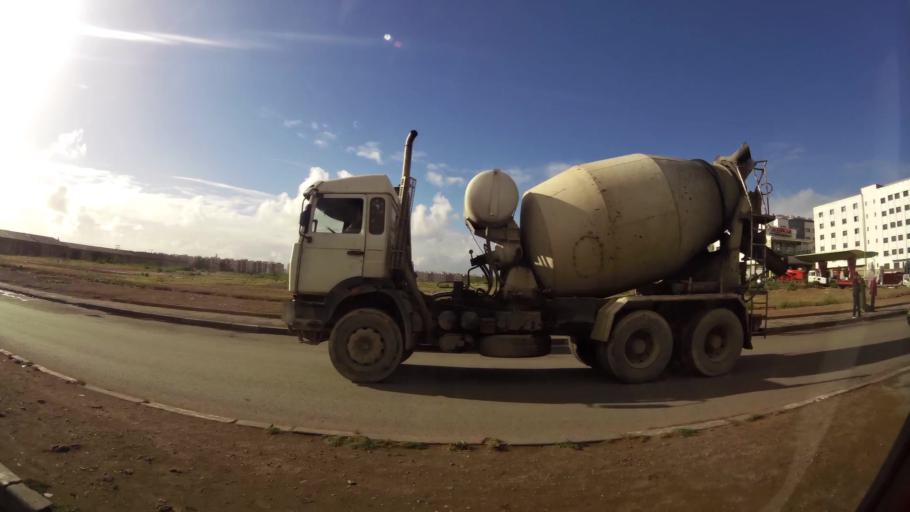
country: MA
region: Grand Casablanca
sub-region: Casablanca
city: Casablanca
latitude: 33.5528
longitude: -7.6912
